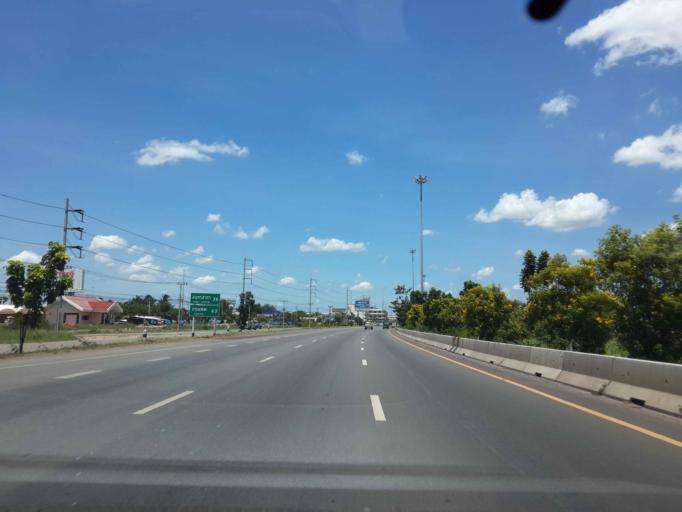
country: TH
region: Samut Songkhram
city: Samut Songkhram
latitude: 13.3998
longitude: 100.0074
